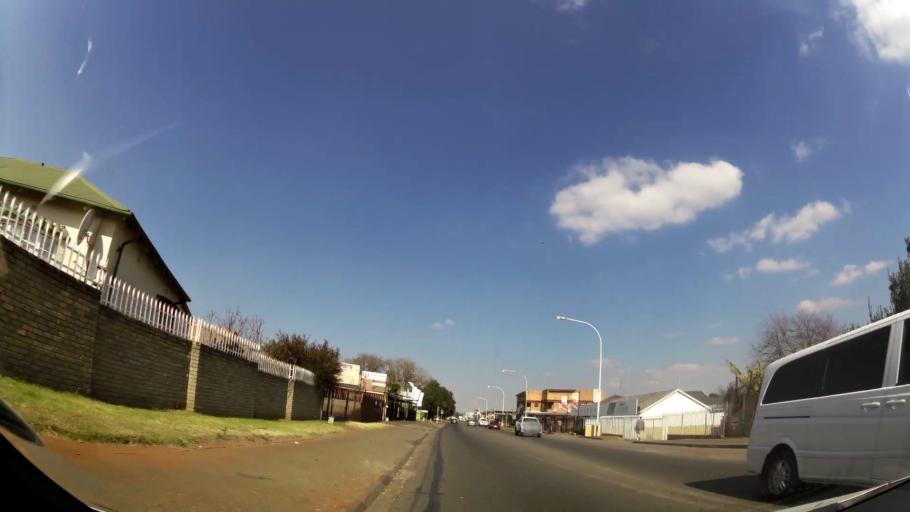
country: ZA
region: Gauteng
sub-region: Ekurhuleni Metropolitan Municipality
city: Germiston
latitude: -26.1842
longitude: 28.2068
